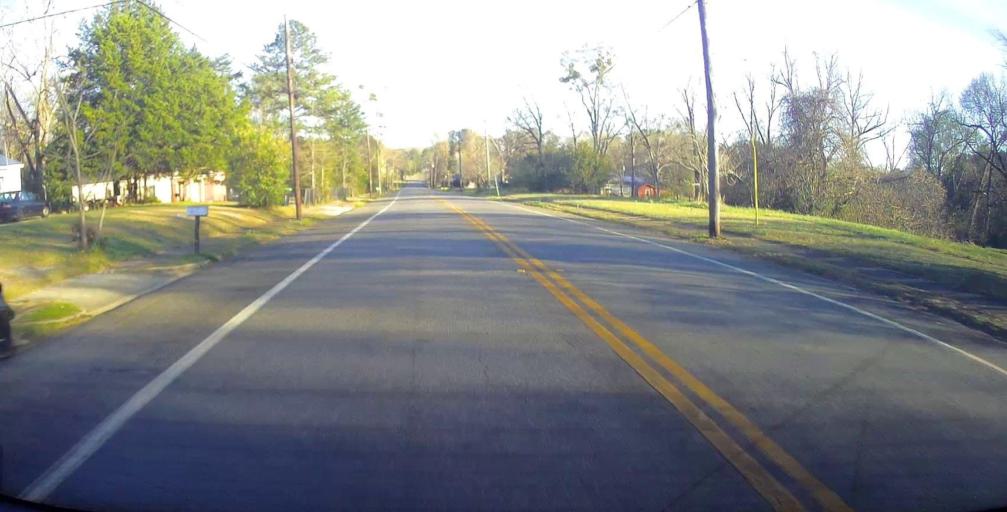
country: US
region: Georgia
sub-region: Talbot County
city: Talbotton
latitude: 32.6723
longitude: -84.5375
